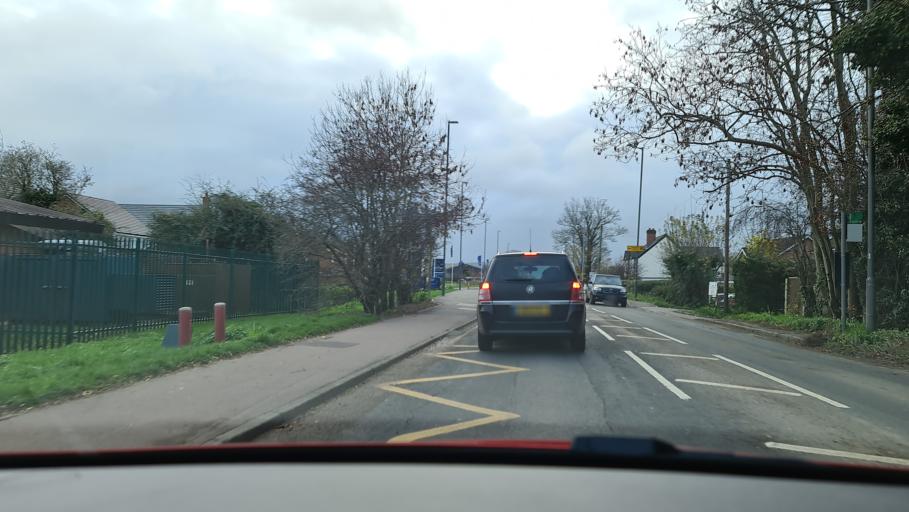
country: GB
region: England
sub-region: Buckinghamshire
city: Aylesbury
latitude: 51.7962
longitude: -0.8043
